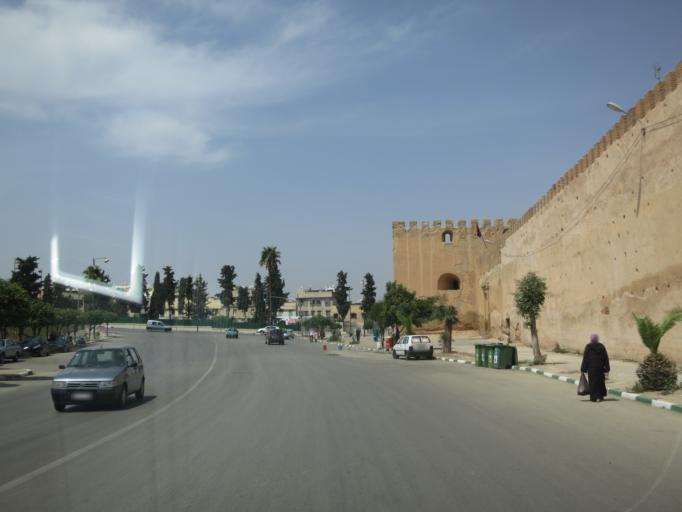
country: MA
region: Meknes-Tafilalet
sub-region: Meknes
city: Meknes
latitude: 33.8869
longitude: -5.5669
